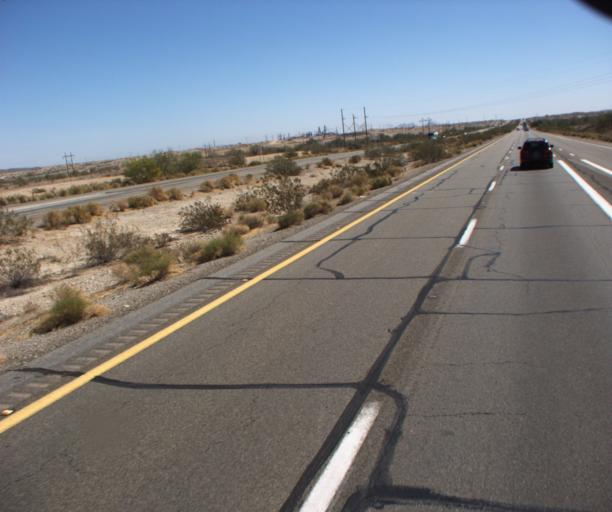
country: US
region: Arizona
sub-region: Yuma County
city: Fortuna Foothills
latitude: 32.6658
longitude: -114.2794
